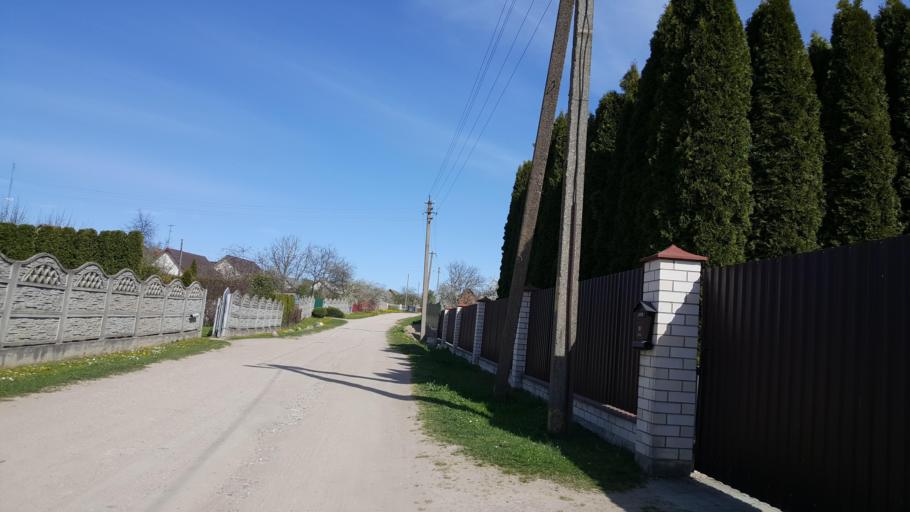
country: BY
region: Brest
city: Vysokaye
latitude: 52.3616
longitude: 23.3844
